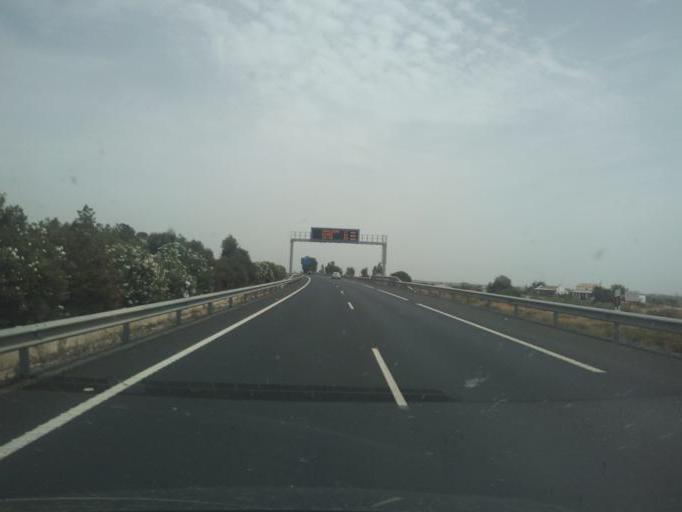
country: ES
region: Andalusia
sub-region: Provincia de Huelva
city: Bollullos par del Condado
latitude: 37.3524
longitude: -6.5764
